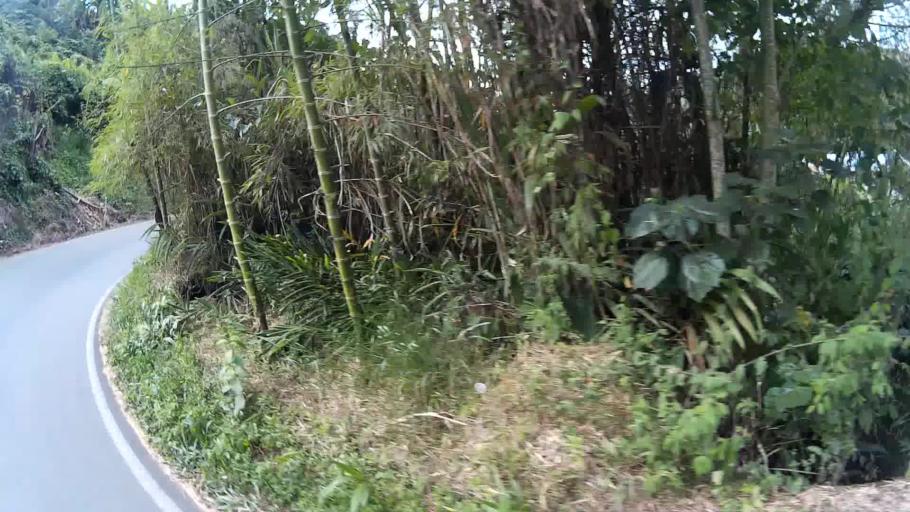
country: CO
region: Risaralda
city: Marsella
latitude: 4.8990
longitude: -75.7357
